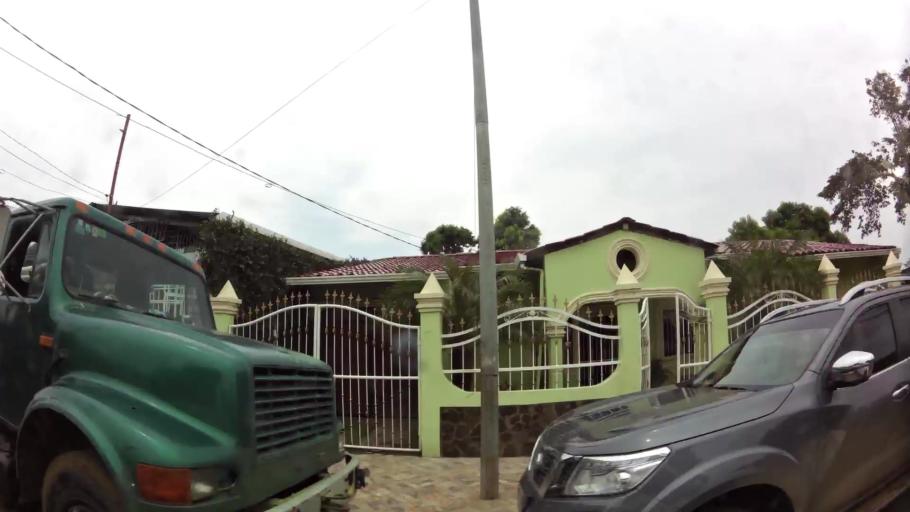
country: NI
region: Granada
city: Nandaime
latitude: 11.7591
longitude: -86.0586
